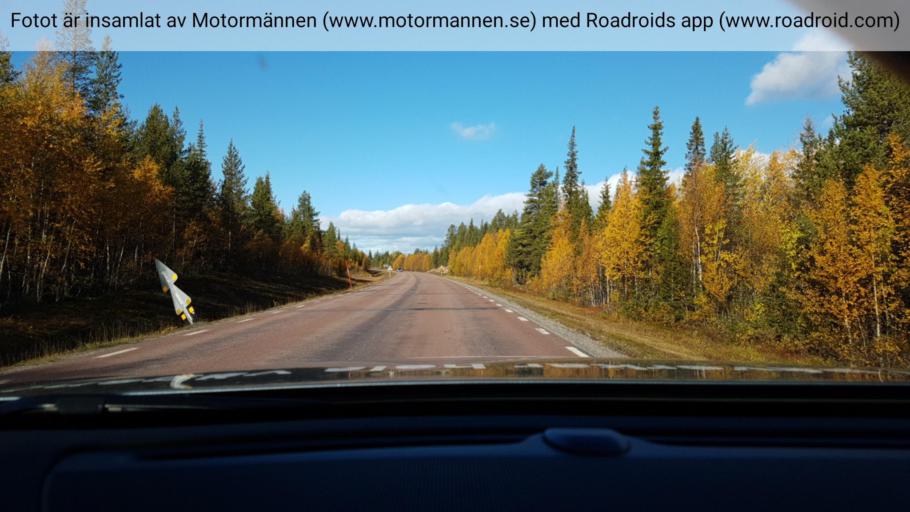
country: SE
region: Norrbotten
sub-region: Arjeplogs Kommun
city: Arjeplog
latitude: 65.9891
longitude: 18.1853
